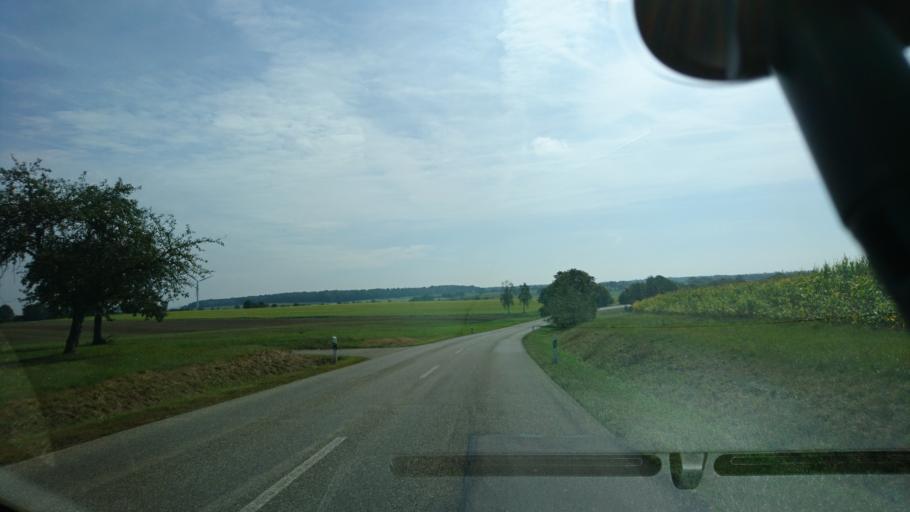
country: DE
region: Baden-Wuerttemberg
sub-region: Regierungsbezirk Stuttgart
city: Wolpertshausen
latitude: 49.1876
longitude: 9.8773
